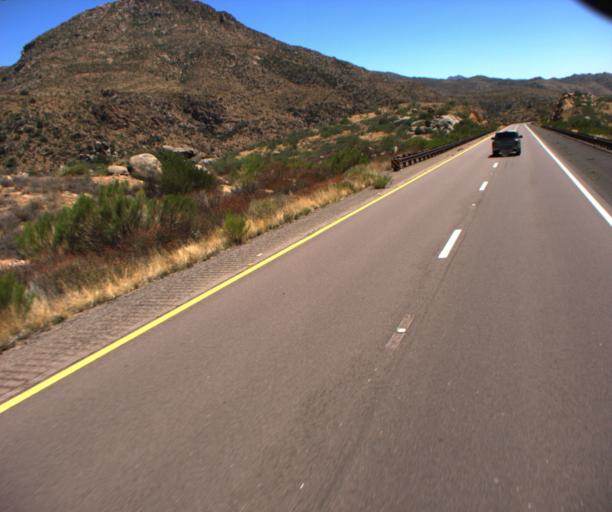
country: US
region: Arizona
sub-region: Gila County
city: Tonto Basin
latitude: 33.8455
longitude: -111.4697
